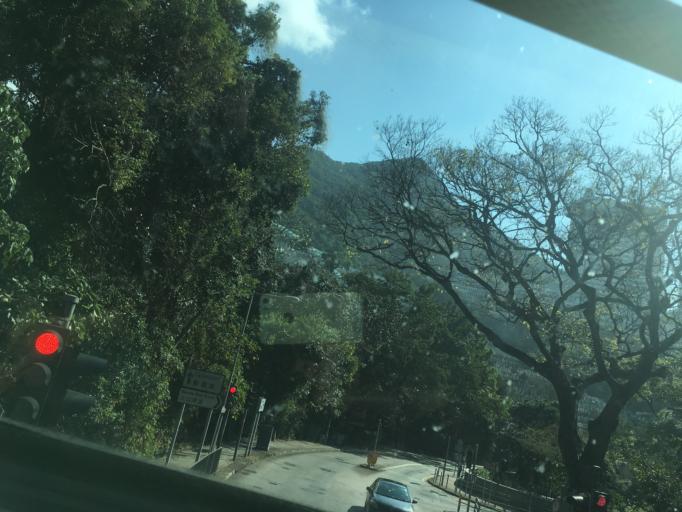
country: HK
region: Central and Western
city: Central
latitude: 22.2732
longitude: 114.1266
